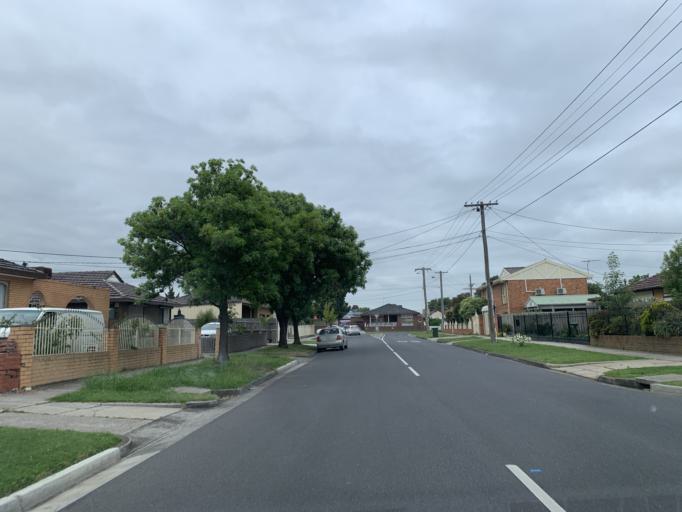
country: AU
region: Victoria
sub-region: Brimbank
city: Kealba
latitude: -37.7470
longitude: 144.8164
